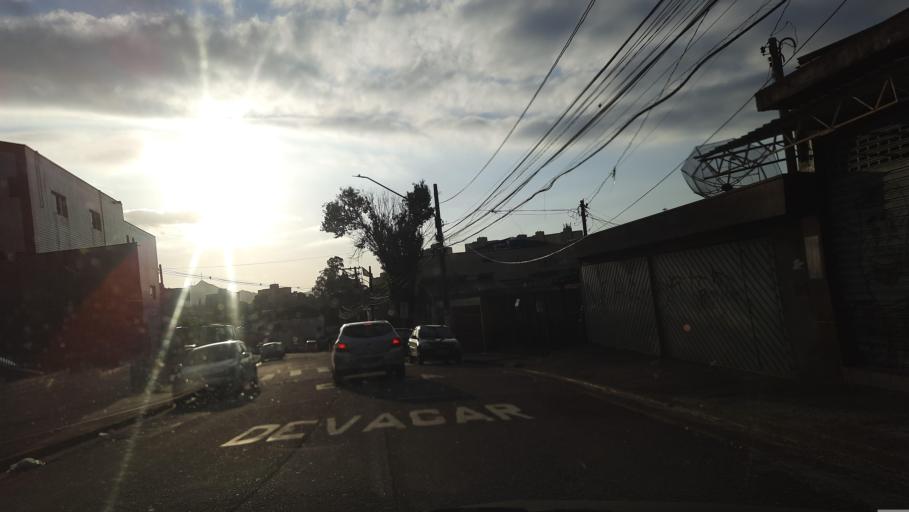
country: BR
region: Sao Paulo
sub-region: Caieiras
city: Caieiras
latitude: -23.4351
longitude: -46.7151
